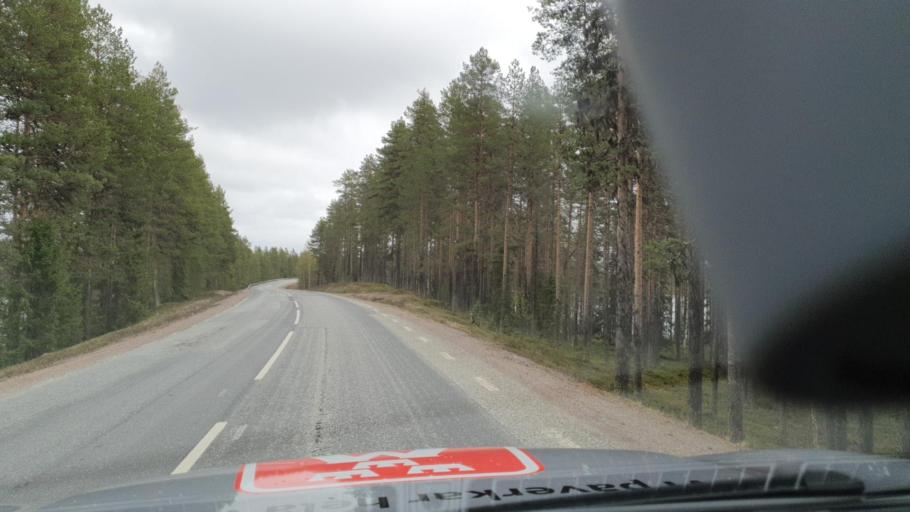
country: SE
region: Vaesternorrland
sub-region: Solleftea Kommun
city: Solleftea
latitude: 63.6470
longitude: 17.3828
